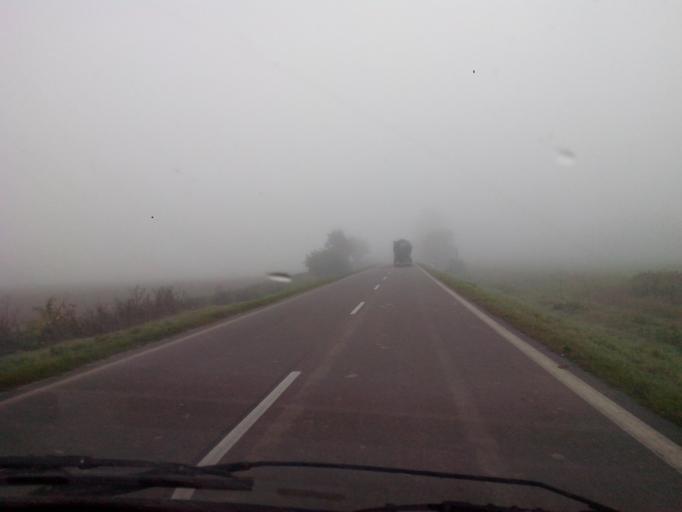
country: PL
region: Subcarpathian Voivodeship
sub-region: Powiat przemyski
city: Krasiczyn
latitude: 49.7986
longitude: 22.6413
